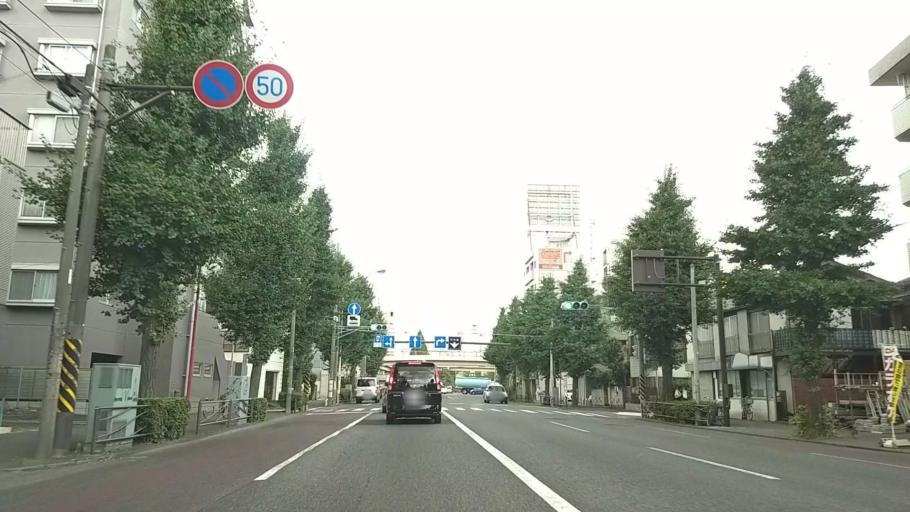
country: JP
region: Kanagawa
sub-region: Kawasaki-shi
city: Kawasaki
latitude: 35.5295
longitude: 139.7156
